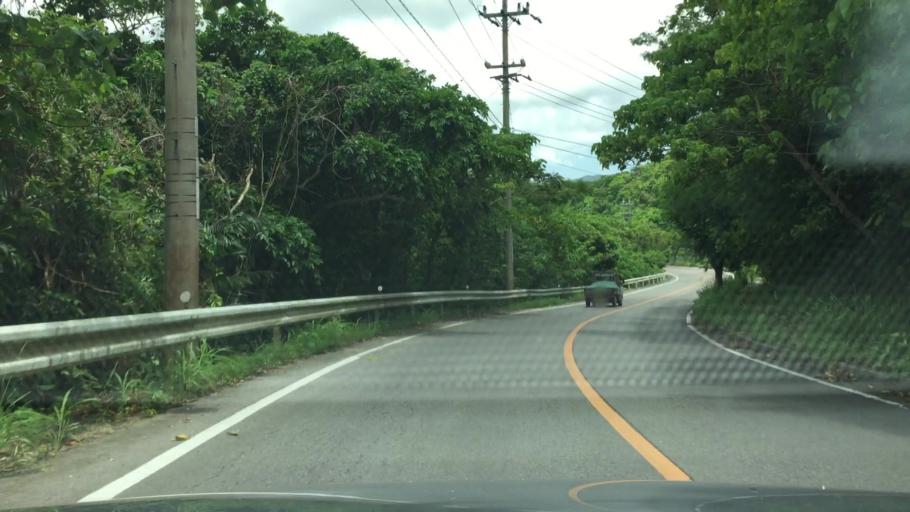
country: JP
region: Okinawa
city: Ishigaki
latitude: 24.3771
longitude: 124.1535
